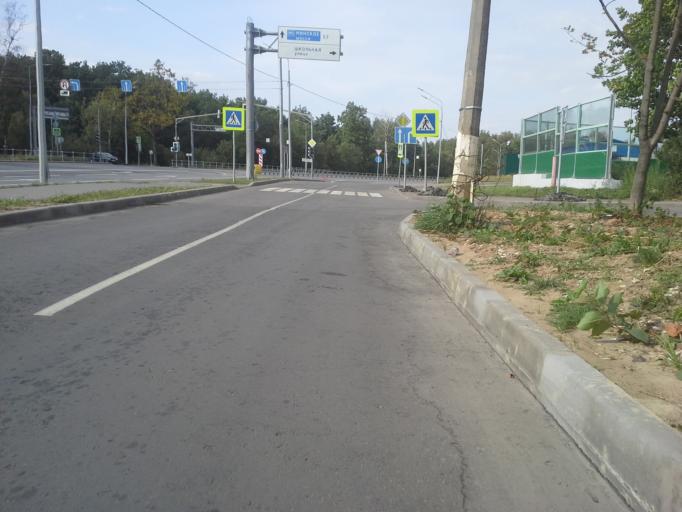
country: RU
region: Moskovskaya
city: Kokoshkino
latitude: 55.5997
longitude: 37.1598
